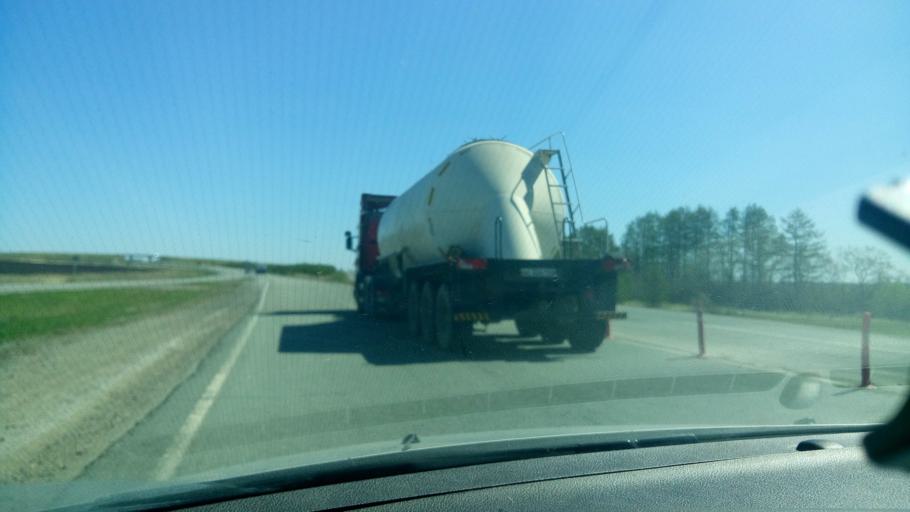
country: RU
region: Sverdlovsk
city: Yelanskiy
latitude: 56.7945
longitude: 62.5128
